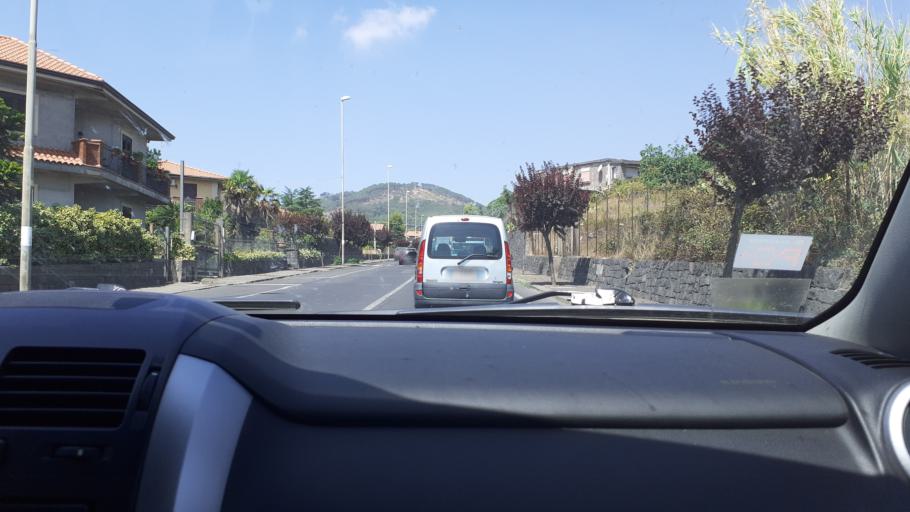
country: IT
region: Sicily
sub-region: Catania
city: Nicolosi
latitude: 37.6163
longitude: 15.0329
